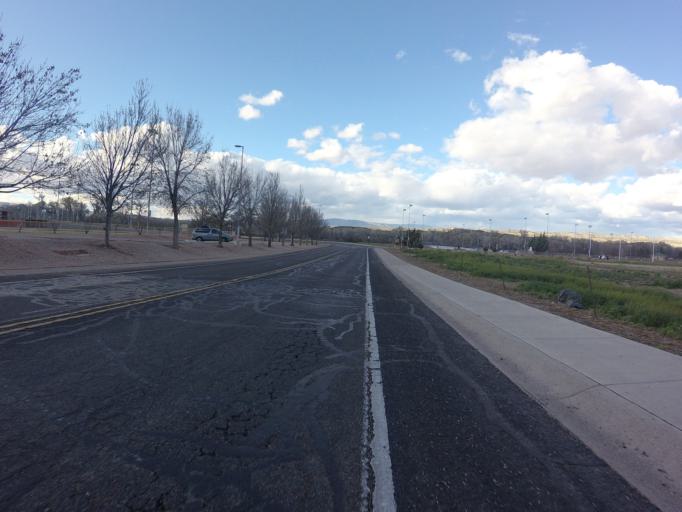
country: US
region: Arizona
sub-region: Yavapai County
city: Cottonwood
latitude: 34.7460
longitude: -112.0165
